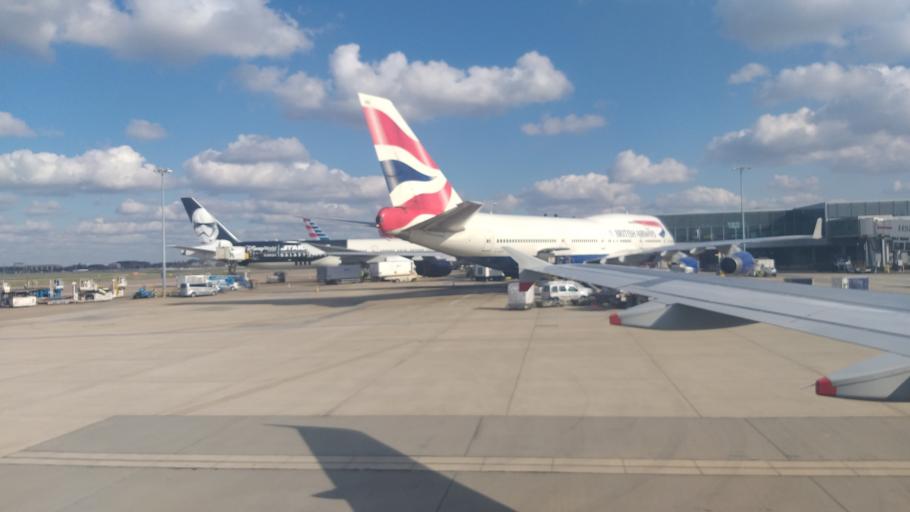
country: GB
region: England
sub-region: Greater London
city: West Drayton
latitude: 51.4739
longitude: -0.4673
